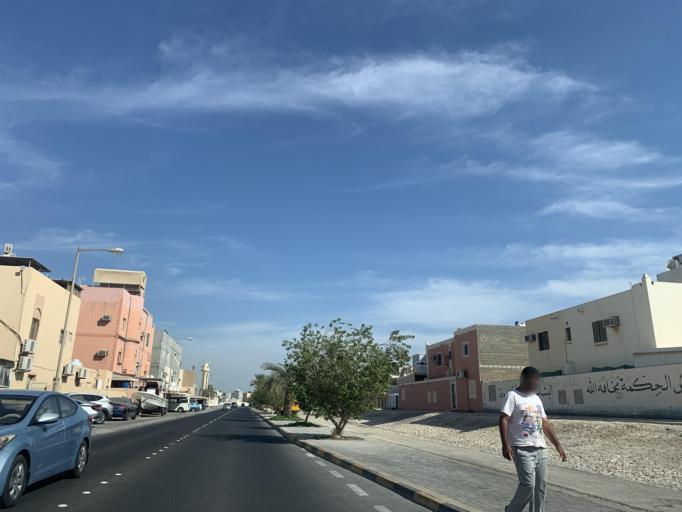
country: BH
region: Central Governorate
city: Madinat Hamad
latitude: 26.1254
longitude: 50.4953
